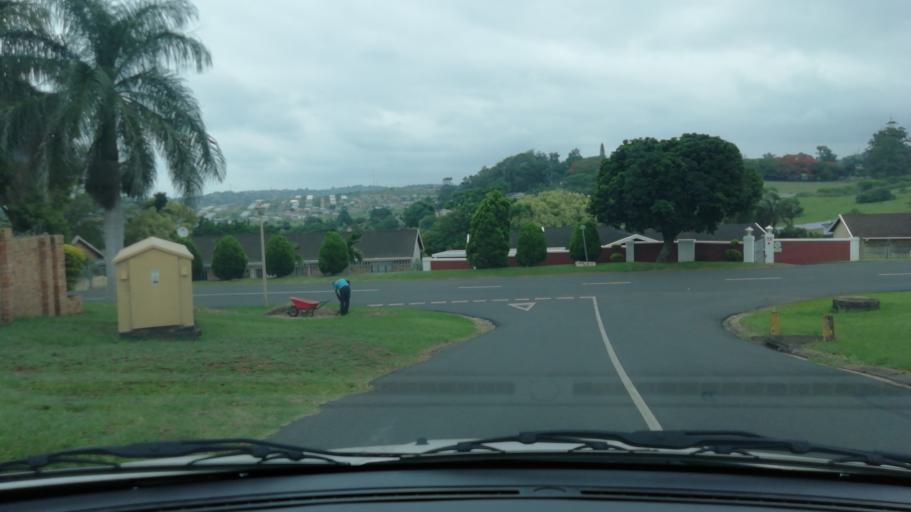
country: ZA
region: KwaZulu-Natal
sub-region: uThungulu District Municipality
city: Empangeni
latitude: -28.7611
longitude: 31.8865
